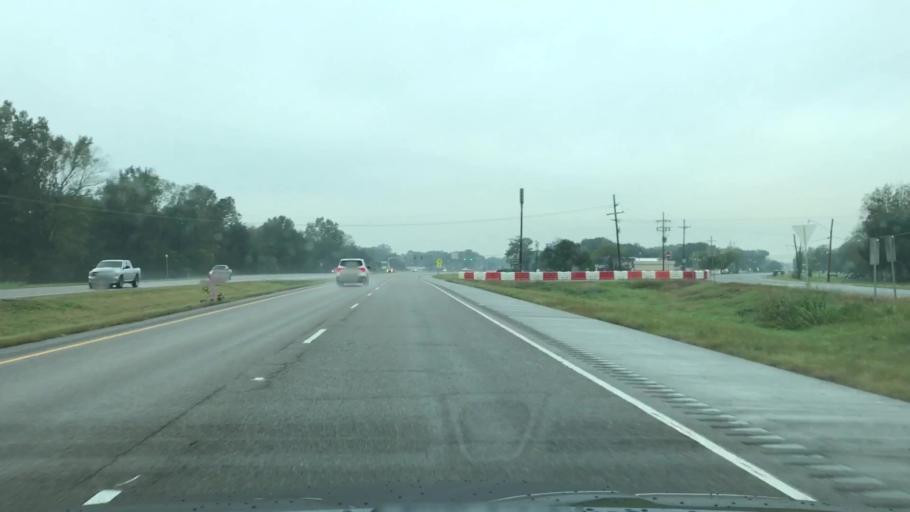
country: US
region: Louisiana
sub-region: Saint Charles Parish
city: Des Allemands
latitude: 29.8266
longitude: -90.4625
